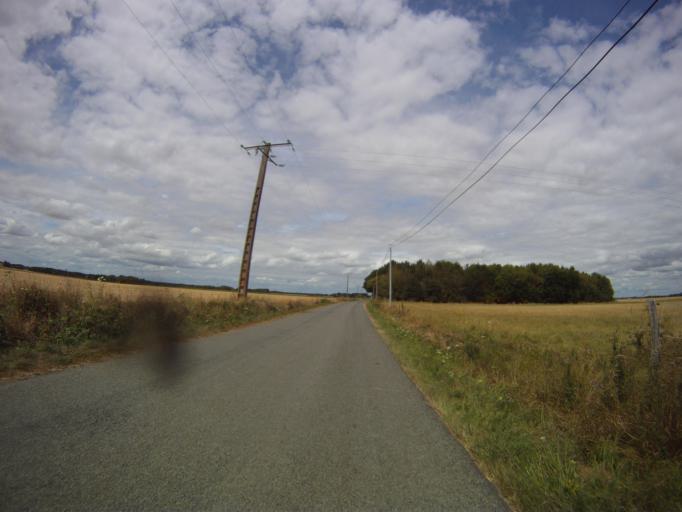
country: FR
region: Centre
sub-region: Departement du Loir-et-Cher
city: Montoire-sur-le-Loir
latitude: 47.6948
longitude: 0.8055
